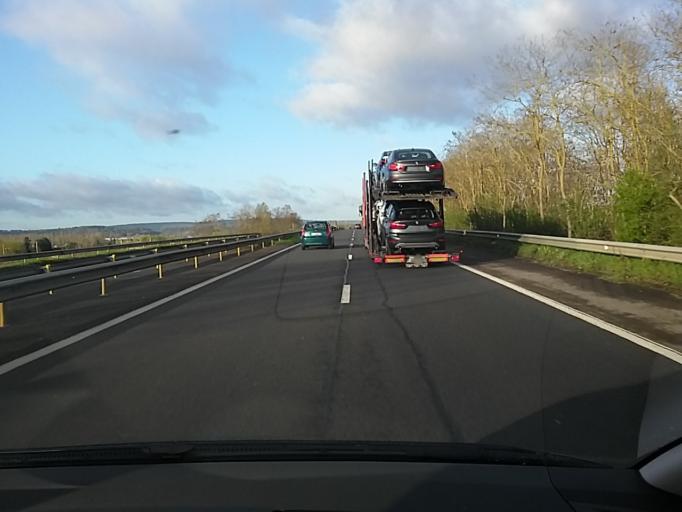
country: FR
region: Picardie
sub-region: Departement de l'Oise
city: Longueil-Sainte-Marie
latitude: 49.3363
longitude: 2.7290
